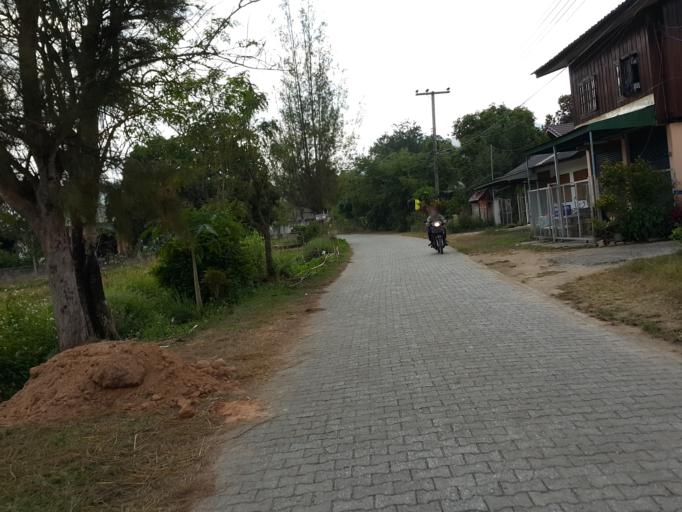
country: TH
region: Chiang Mai
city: Mae On
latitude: 18.7172
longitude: 99.2016
